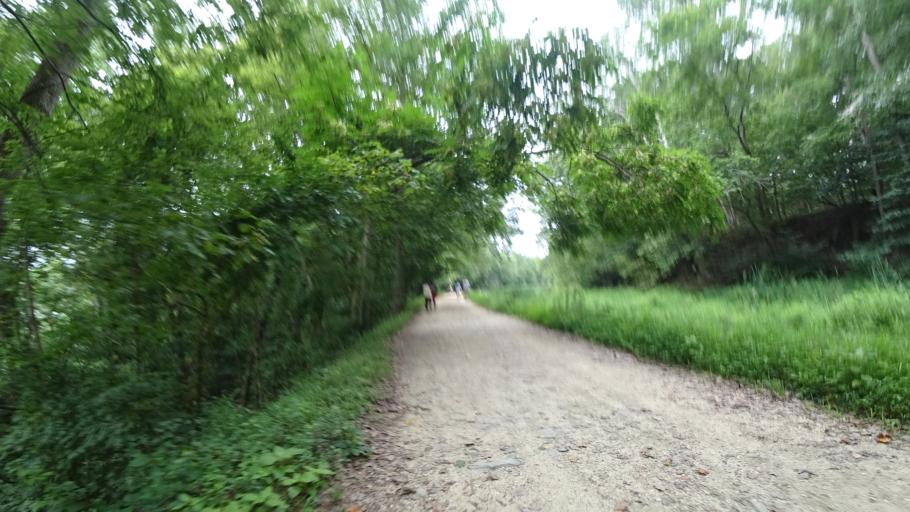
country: US
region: Maryland
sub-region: Montgomery County
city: Potomac
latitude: 38.9779
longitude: -77.2117
